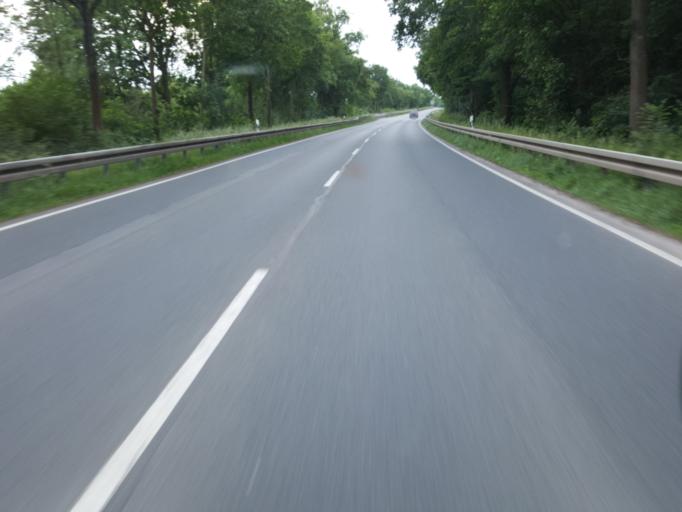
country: DE
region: Lower Saxony
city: Stolzenau
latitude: 52.5080
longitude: 9.0701
